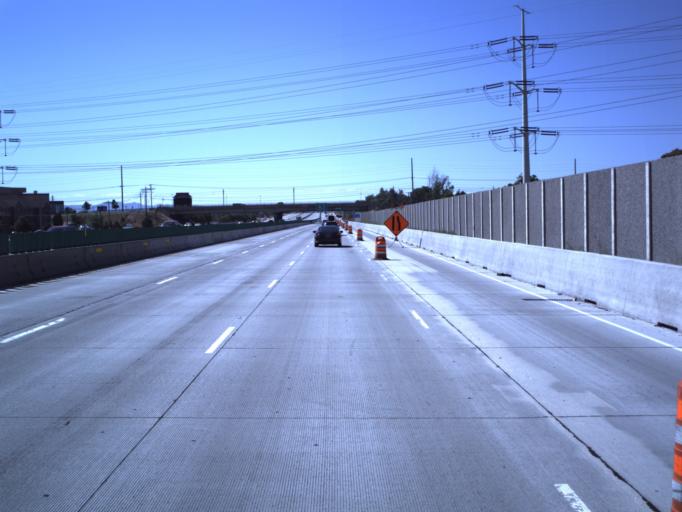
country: US
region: Utah
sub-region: Salt Lake County
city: Taylorsville
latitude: 40.7073
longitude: -111.9536
